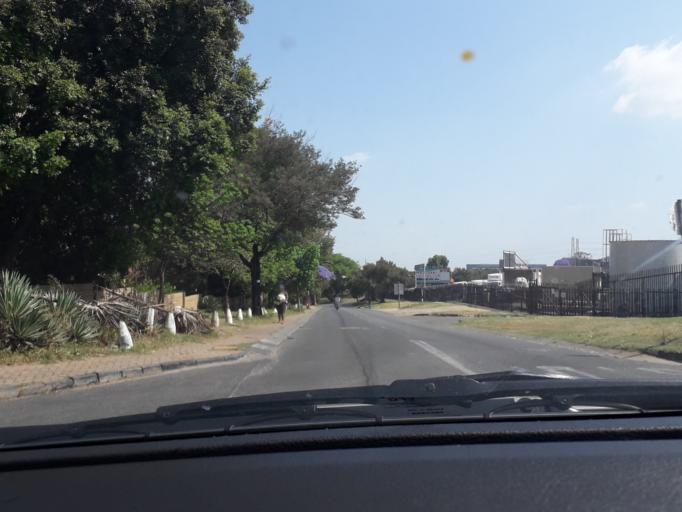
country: ZA
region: Gauteng
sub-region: City of Johannesburg Metropolitan Municipality
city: Modderfontein
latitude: -26.1191
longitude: 28.0832
